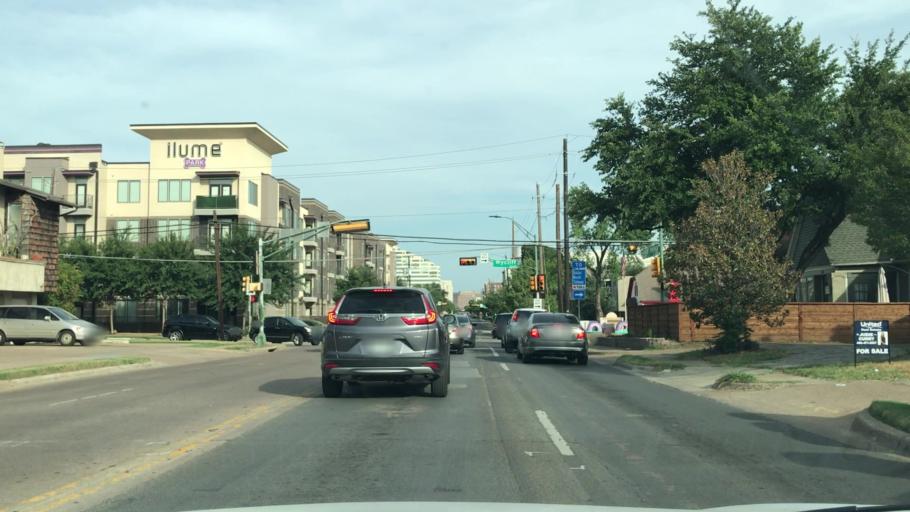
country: US
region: Texas
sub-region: Dallas County
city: Highland Park
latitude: 32.8142
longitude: -96.8153
